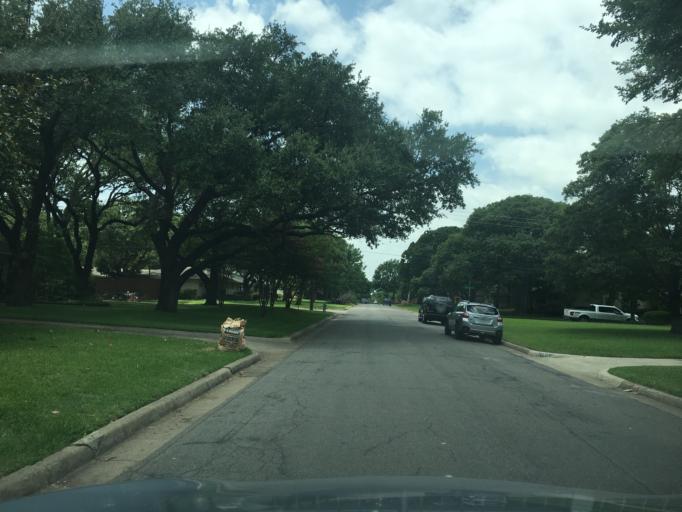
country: US
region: Texas
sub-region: Dallas County
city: Addison
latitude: 32.9043
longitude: -96.8338
